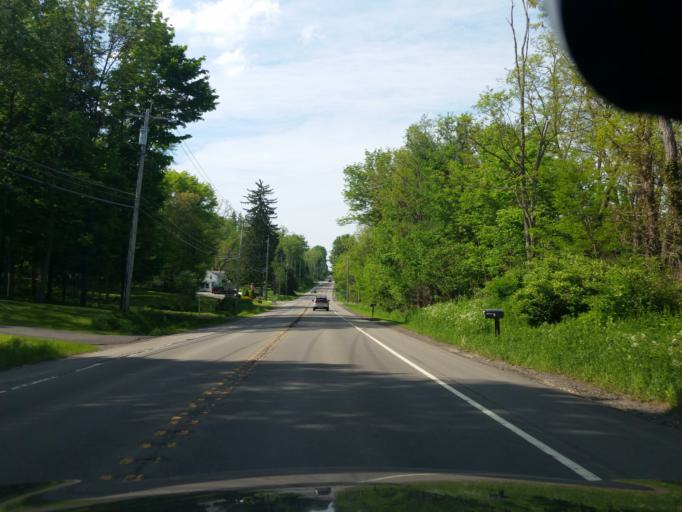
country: US
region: New York
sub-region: Chautauqua County
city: Lakewood
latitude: 42.1166
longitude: -79.3885
